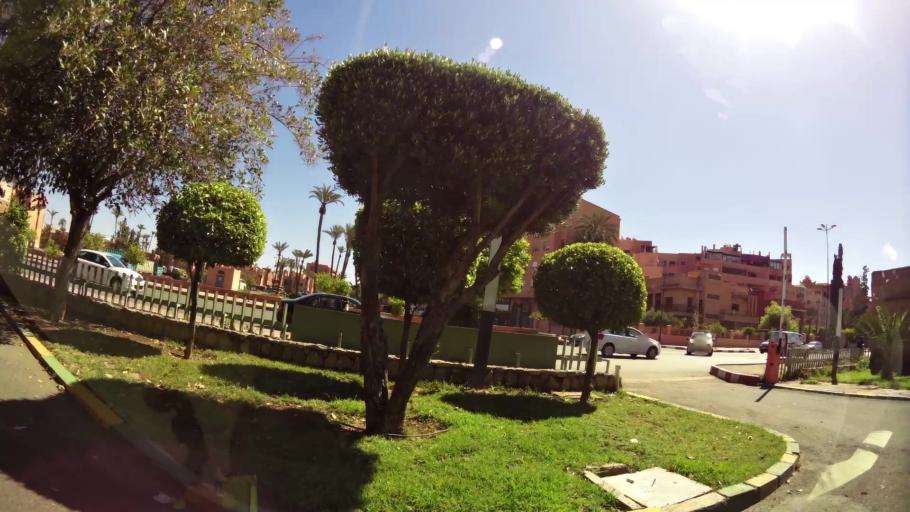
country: MA
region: Marrakech-Tensift-Al Haouz
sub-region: Marrakech
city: Marrakesh
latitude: 31.6410
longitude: -8.0063
